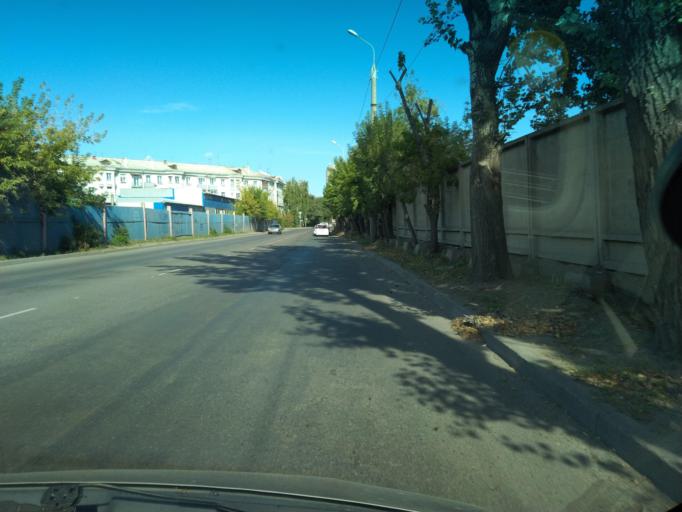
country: RU
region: Krasnoyarskiy
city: Krasnoyarsk
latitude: 56.0089
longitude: 92.9714
